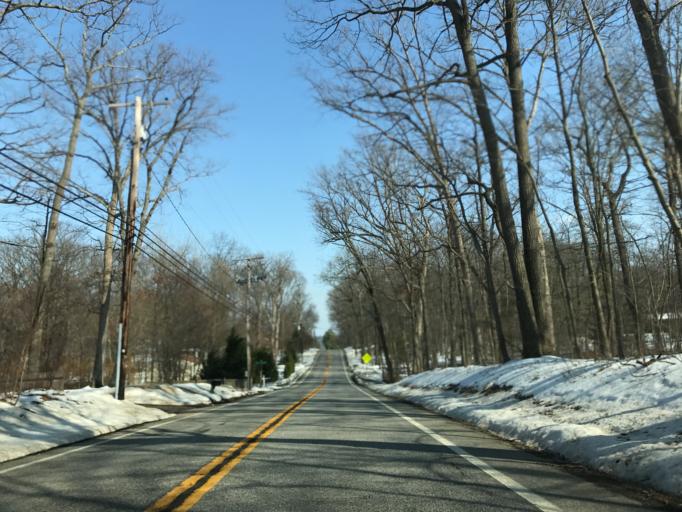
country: US
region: Maryland
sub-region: Harford County
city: Jarrettsville
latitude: 39.7008
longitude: -76.4827
